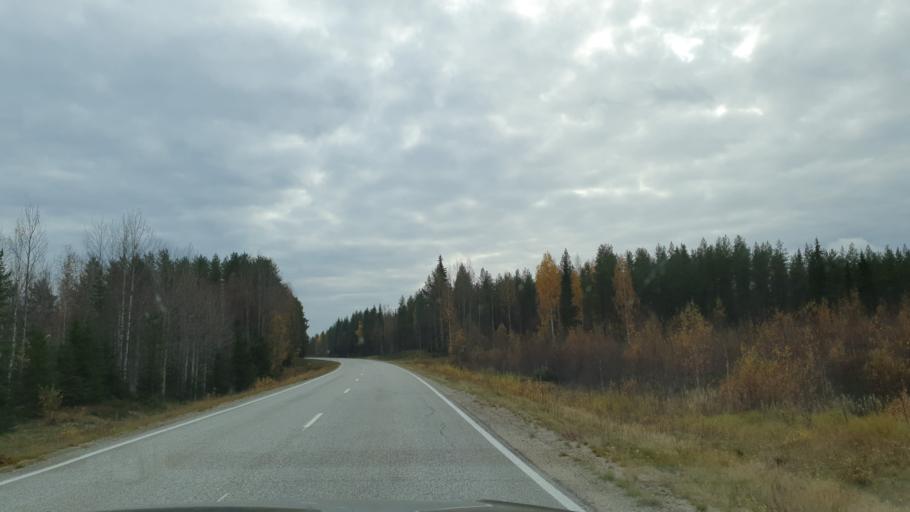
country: FI
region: Kainuu
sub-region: Kehys-Kainuu
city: Puolanka
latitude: 65.2439
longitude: 27.5810
